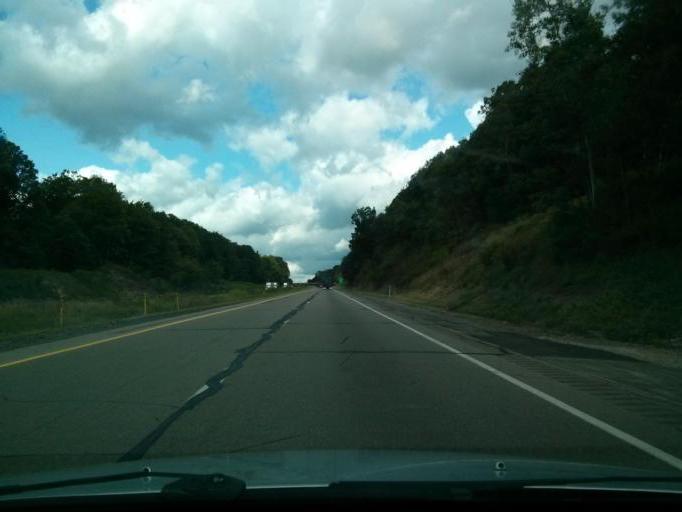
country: US
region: Pennsylvania
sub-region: Jefferson County
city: Brookville
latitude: 41.1635
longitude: -79.0051
